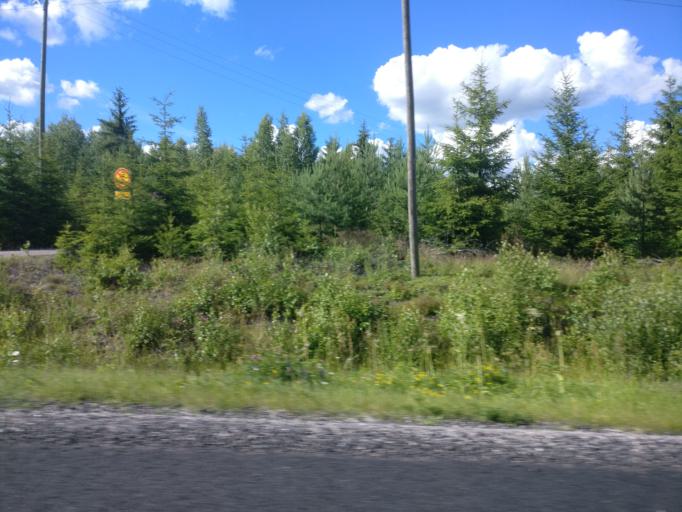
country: FI
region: Uusimaa
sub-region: Helsinki
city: Hyvinge
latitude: 60.6178
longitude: 24.9590
